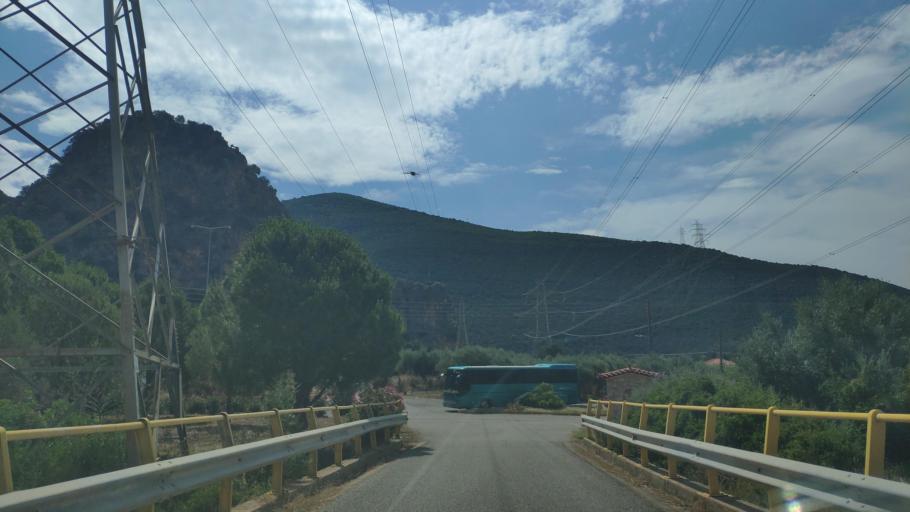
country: GR
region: West Greece
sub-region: Nomos Achaias
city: Selianitika
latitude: 38.3696
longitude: 22.1254
